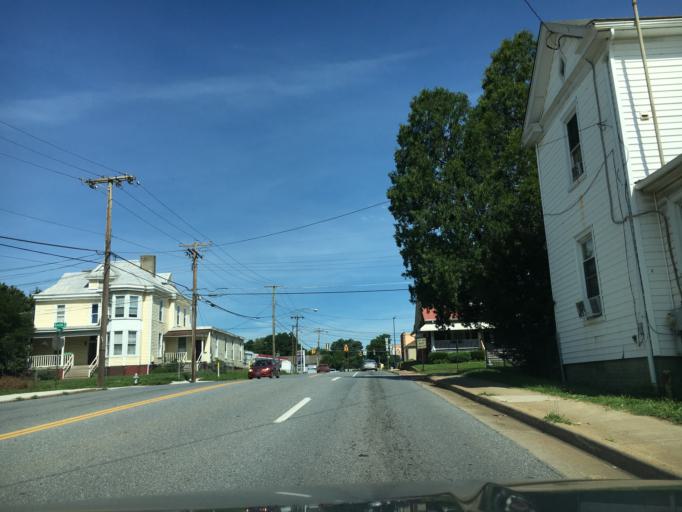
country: US
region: Virginia
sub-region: City of Lynchburg
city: West Lynchburg
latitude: 37.3973
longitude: -79.1685
